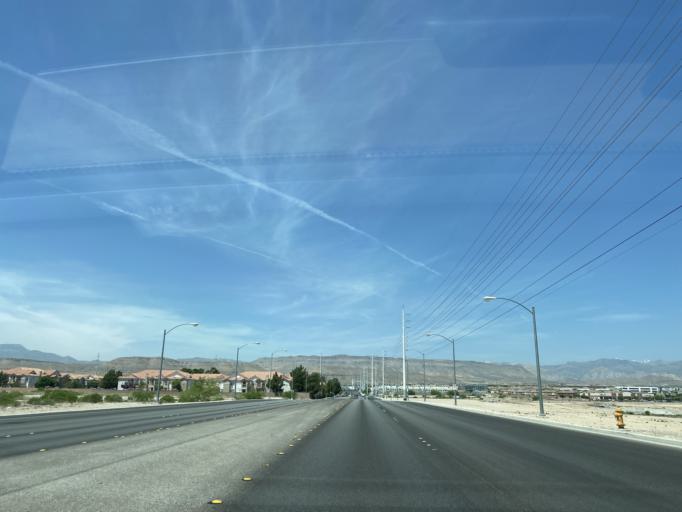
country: US
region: Nevada
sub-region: Clark County
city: Spring Valley
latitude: 36.0852
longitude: -115.2733
